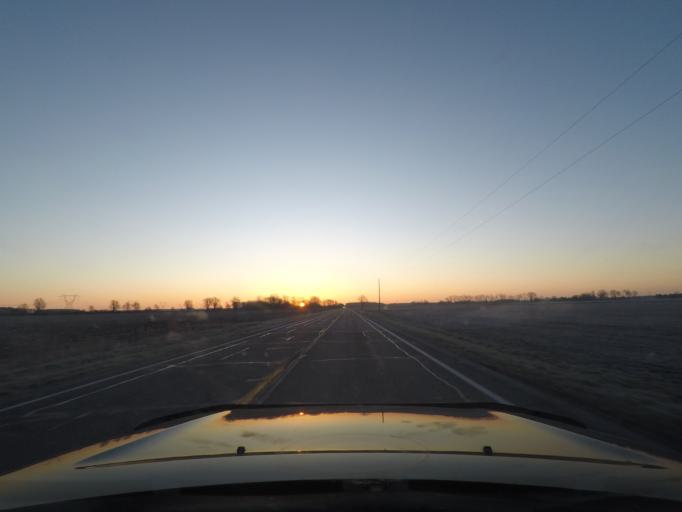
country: US
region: Indiana
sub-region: Saint Joseph County
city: Walkerton
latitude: 41.4763
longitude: -86.5720
